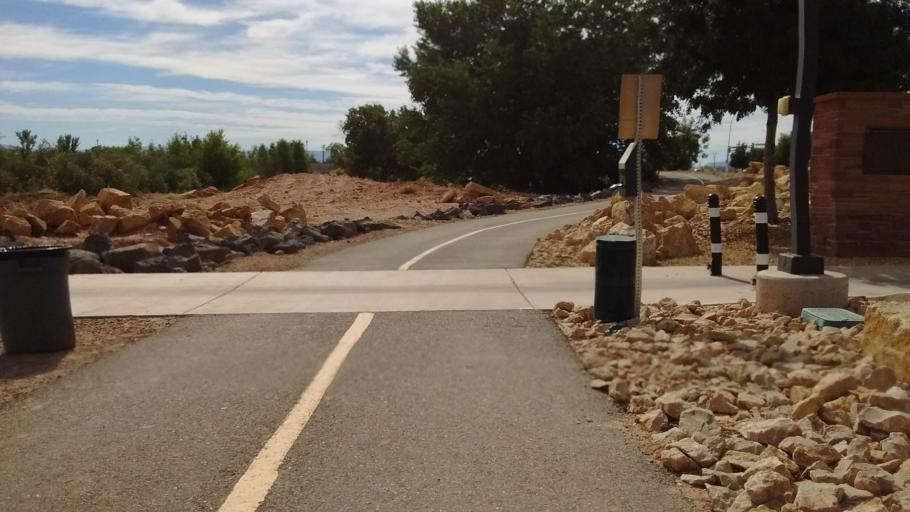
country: US
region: Utah
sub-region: Washington County
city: Washington
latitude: 37.1181
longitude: -113.5004
